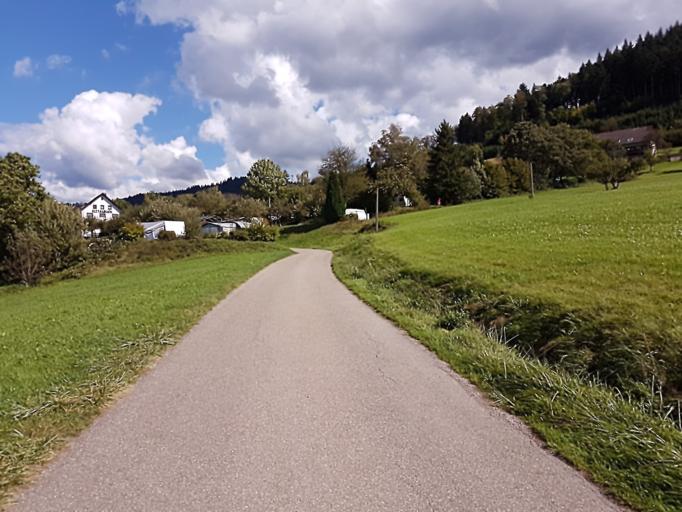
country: DE
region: Baden-Wuerttemberg
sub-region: Freiburg Region
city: Gutach im Breisgau
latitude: 48.1015
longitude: 7.9894
